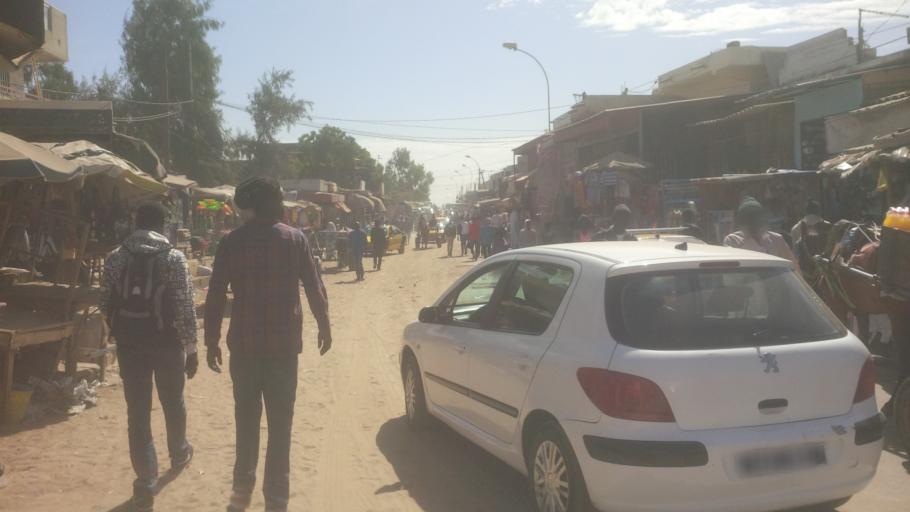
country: SN
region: Dakar
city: Pikine
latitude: 14.7762
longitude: -17.3724
